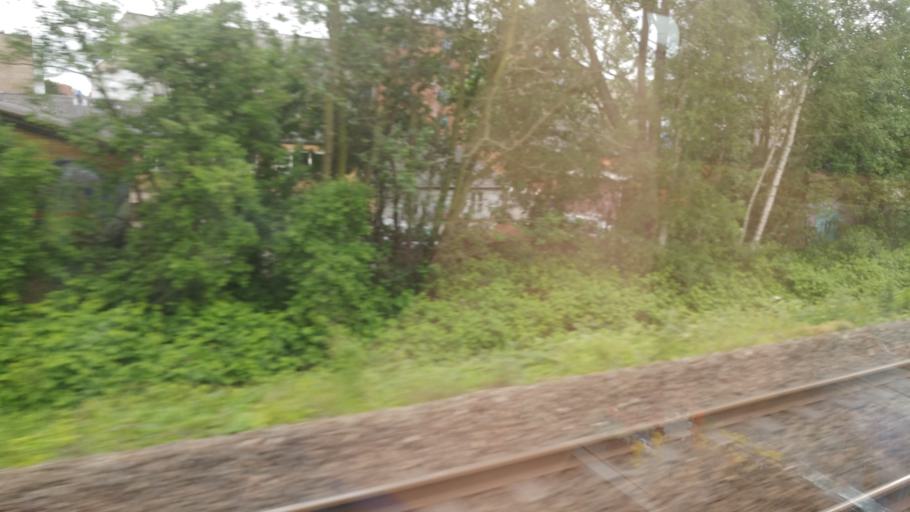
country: DK
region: South Denmark
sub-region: Odense Kommune
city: Odense
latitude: 55.4023
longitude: 10.4105
